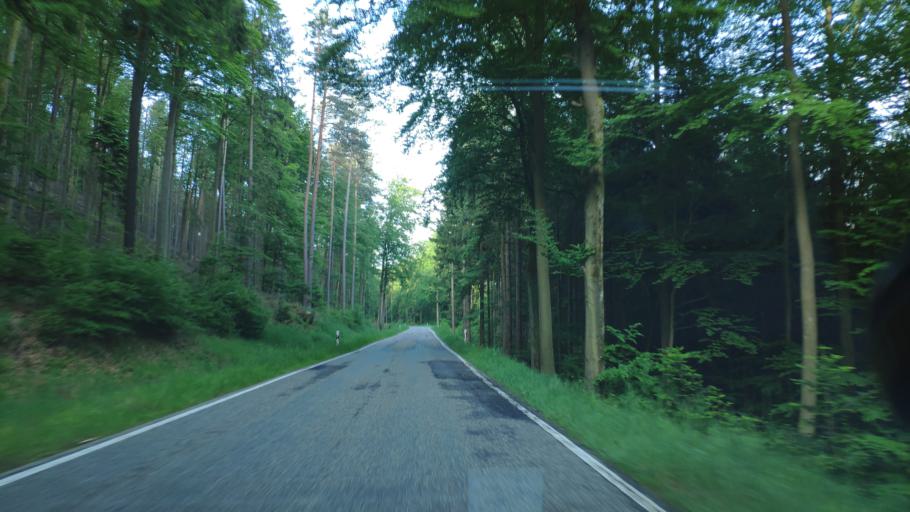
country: DE
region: Rheinland-Pfalz
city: Lemberg
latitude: 49.1277
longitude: 7.6834
